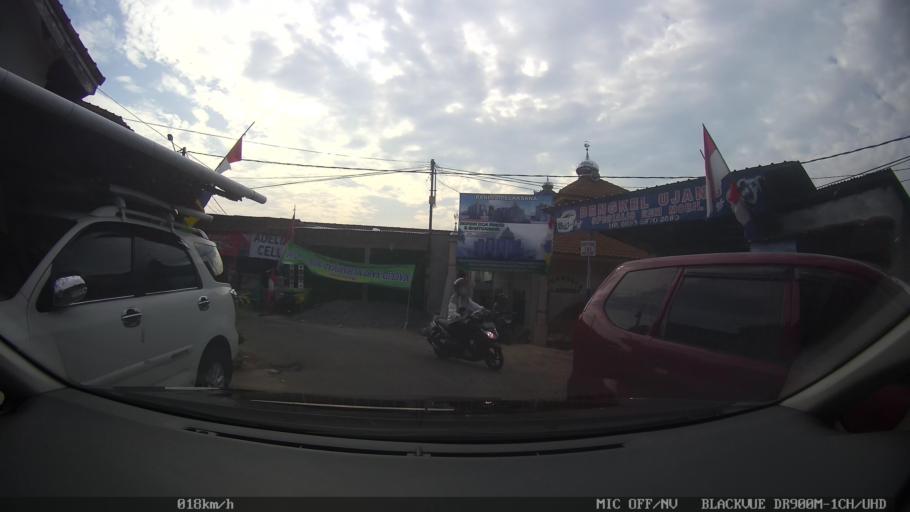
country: ID
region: Lampung
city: Bandarlampung
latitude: -5.4134
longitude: 105.2643
